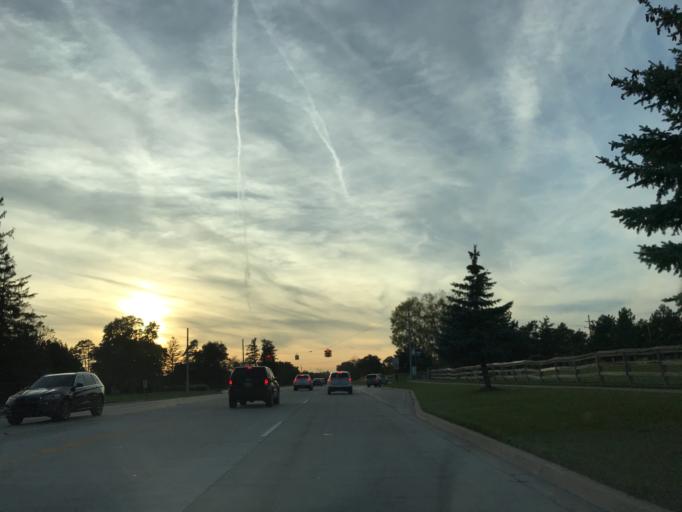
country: US
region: Michigan
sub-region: Oakland County
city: Farmington
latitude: 42.4401
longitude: -83.3954
